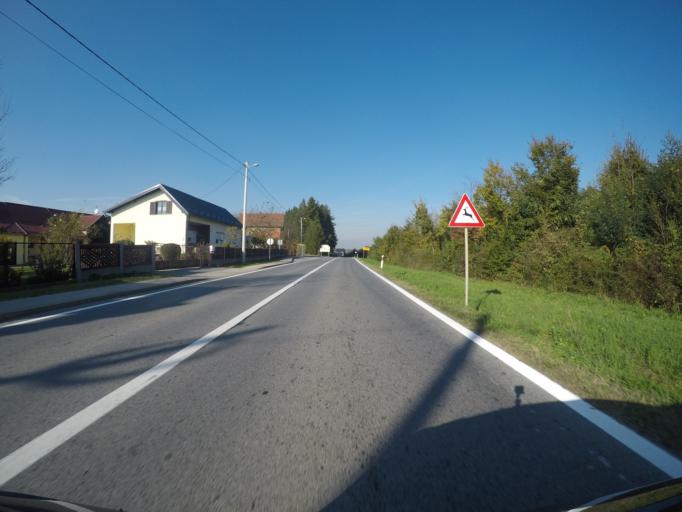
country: HR
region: Bjelovarsko-Bilogorska
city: Bjelovar
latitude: 45.9563
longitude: 16.8922
